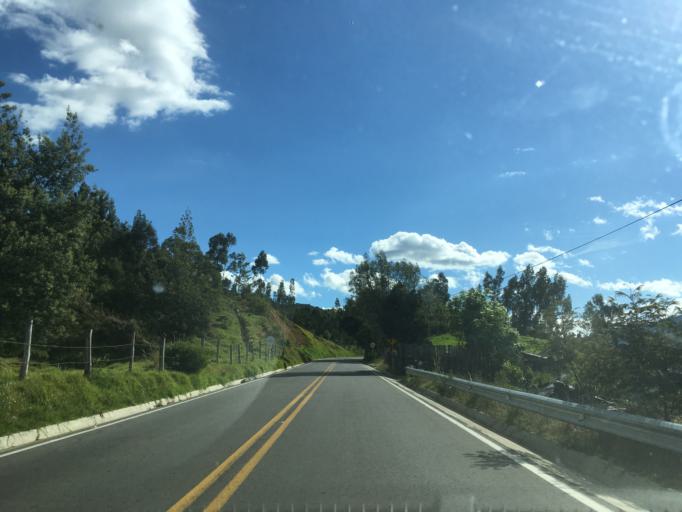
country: CO
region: Boyaca
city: Pesca
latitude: 5.5882
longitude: -73.0310
